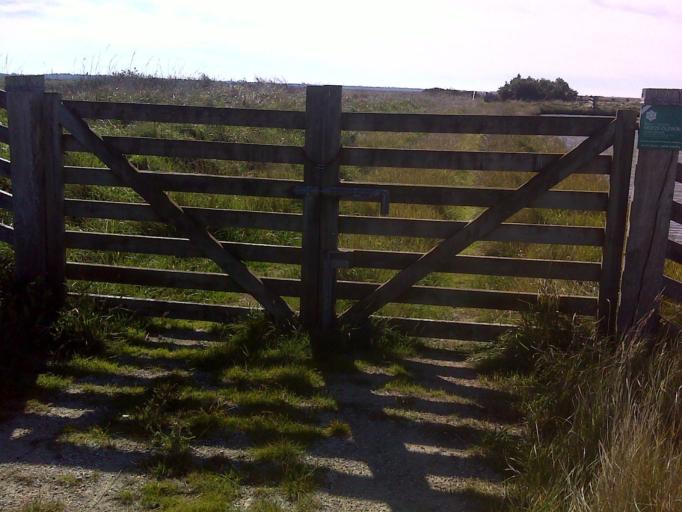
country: FR
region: Poitou-Charentes
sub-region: Departement de la Charente-Maritime
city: Port-des-Barques
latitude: 45.8971
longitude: -1.0767
